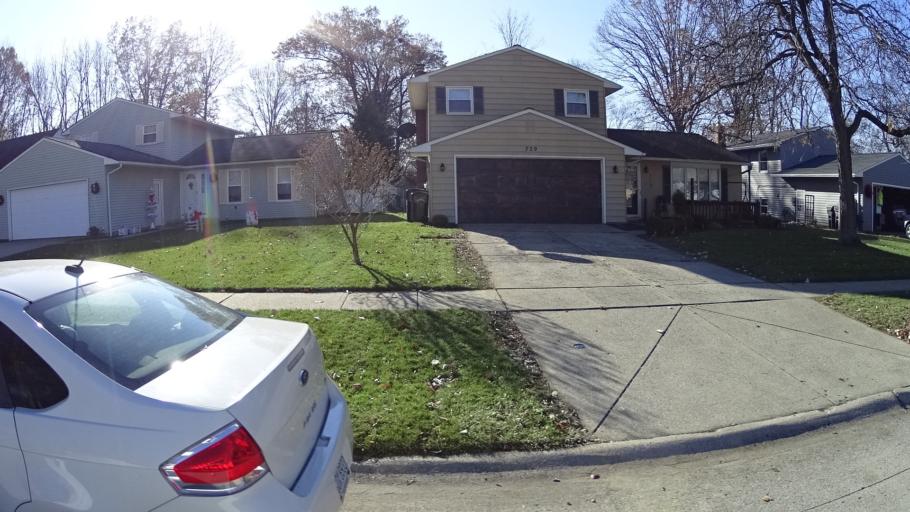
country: US
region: Ohio
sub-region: Lorain County
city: Sheffield
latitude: 41.3917
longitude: -82.0760
